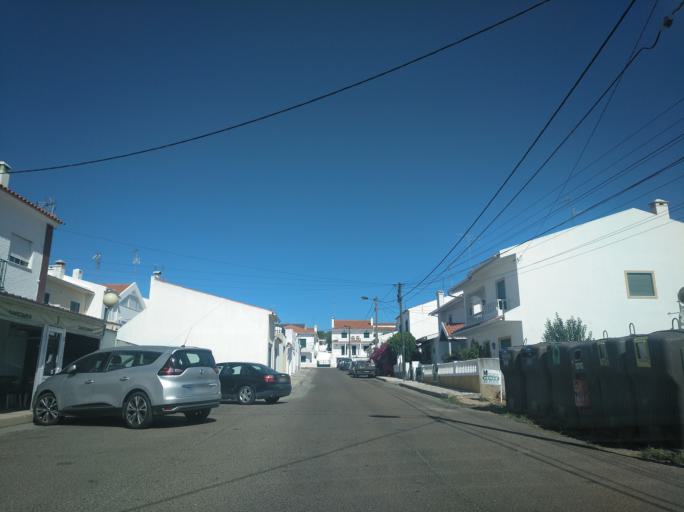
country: PT
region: Portalegre
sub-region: Campo Maior
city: Campo Maior
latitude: 39.0177
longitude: -7.0602
